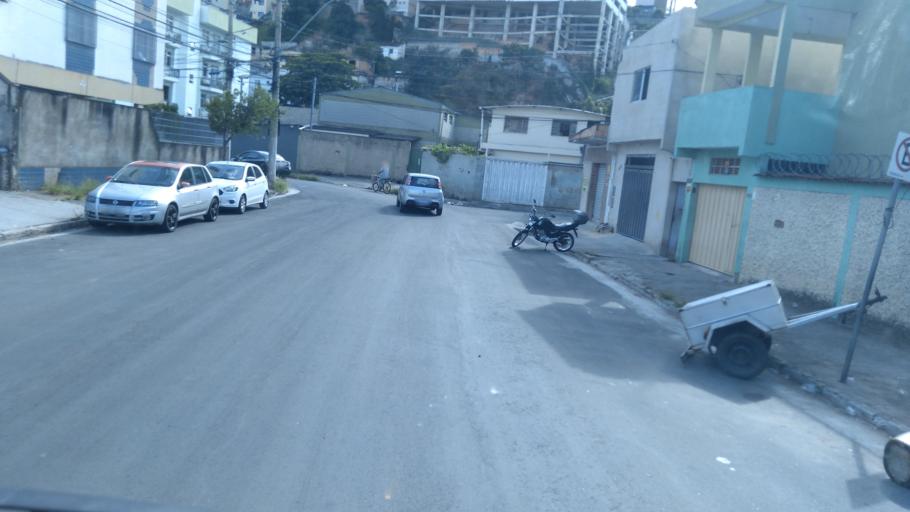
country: BR
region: Minas Gerais
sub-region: Belo Horizonte
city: Belo Horizonte
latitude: -19.9196
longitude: -43.9843
